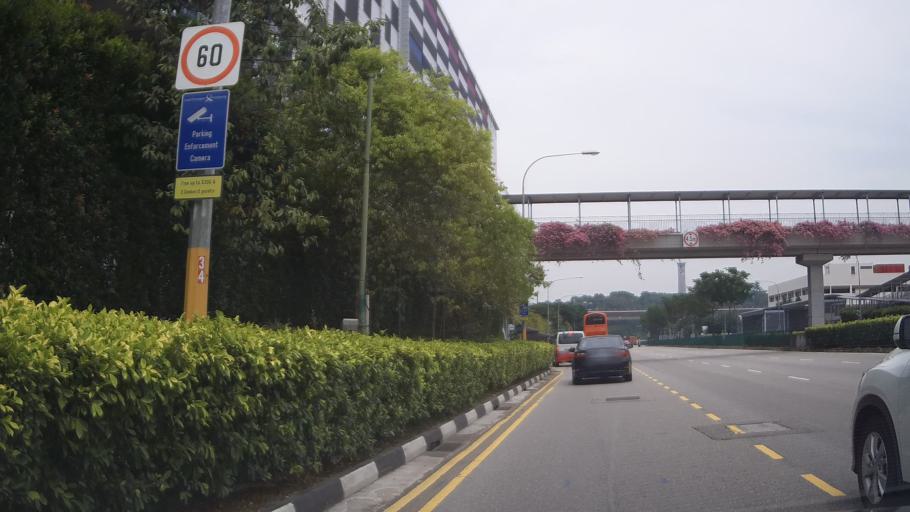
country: MY
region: Johor
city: Johor Bahru
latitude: 1.3247
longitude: 103.6791
